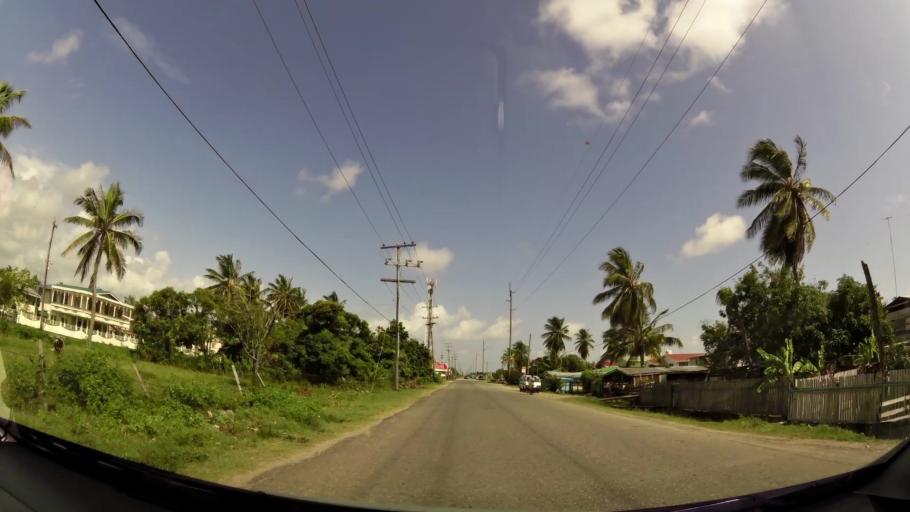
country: GY
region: Demerara-Mahaica
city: Mahaica Village
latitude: 6.7609
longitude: -57.9907
